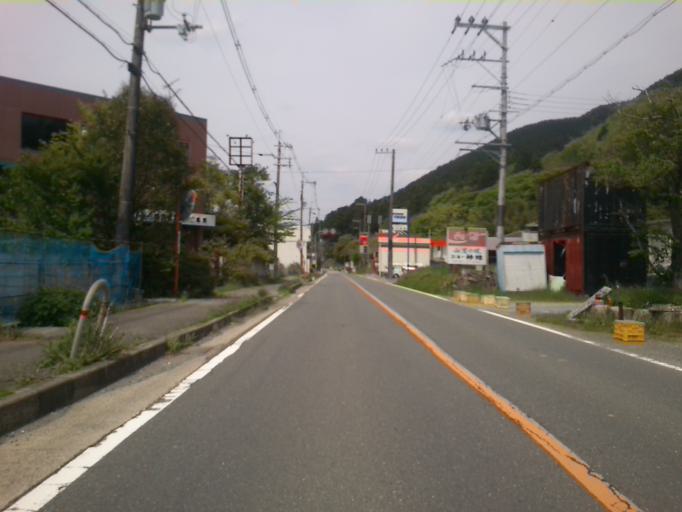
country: JP
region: Kyoto
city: Kameoka
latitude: 34.9414
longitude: 135.4962
